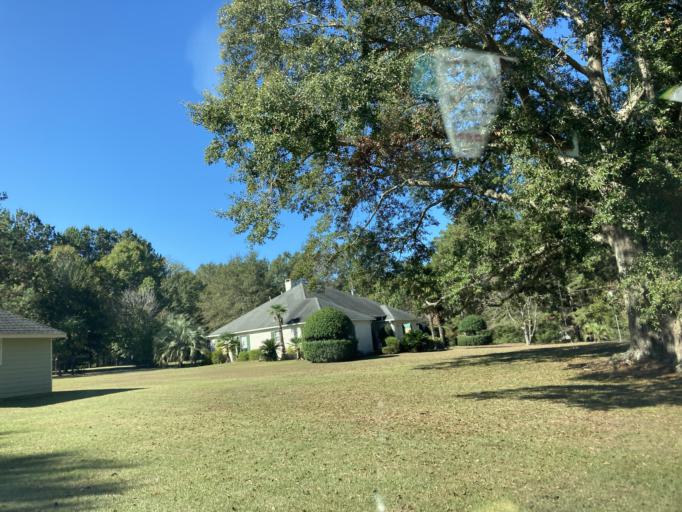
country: US
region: Mississippi
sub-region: Lamar County
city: West Hattiesburg
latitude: 31.3017
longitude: -89.4226
